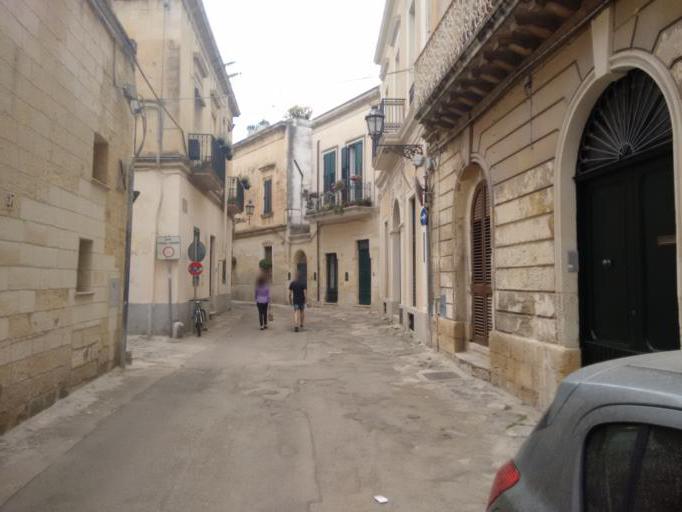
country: IT
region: Apulia
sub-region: Provincia di Lecce
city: Lecce
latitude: 40.3544
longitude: 18.1672
